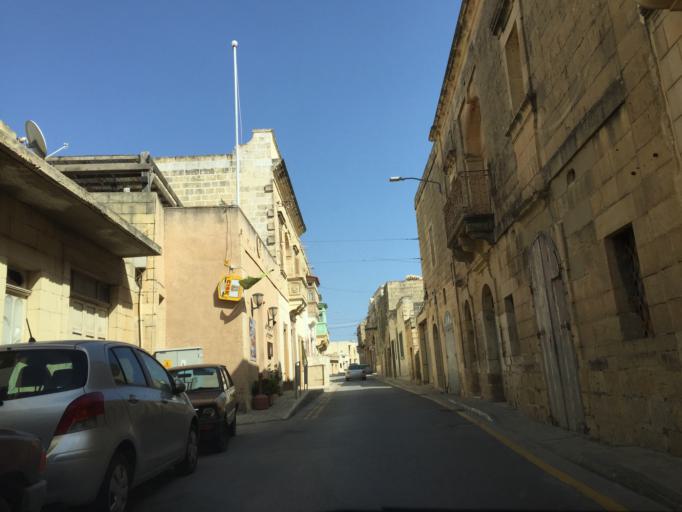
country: MT
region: L-Gharb
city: Gharb
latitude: 36.0592
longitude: 14.2097
